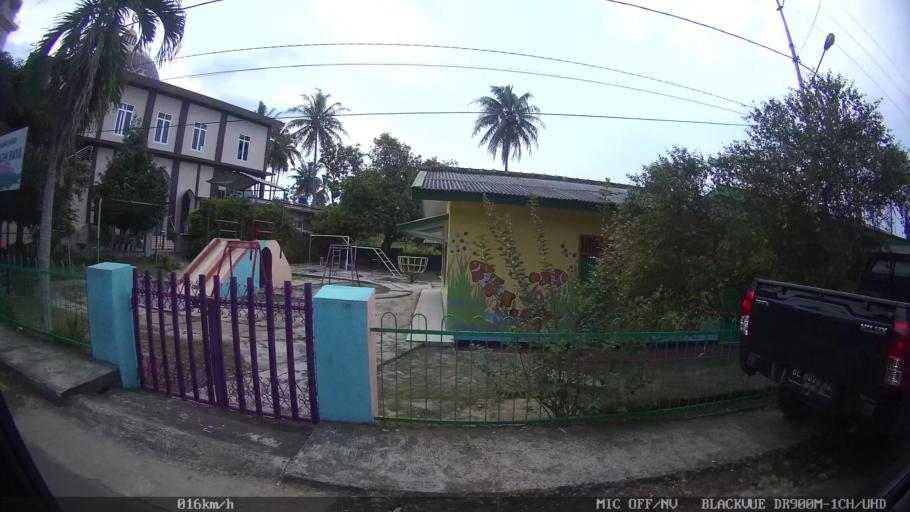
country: ID
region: Lampung
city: Kedaton
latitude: -5.3963
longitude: 105.2130
